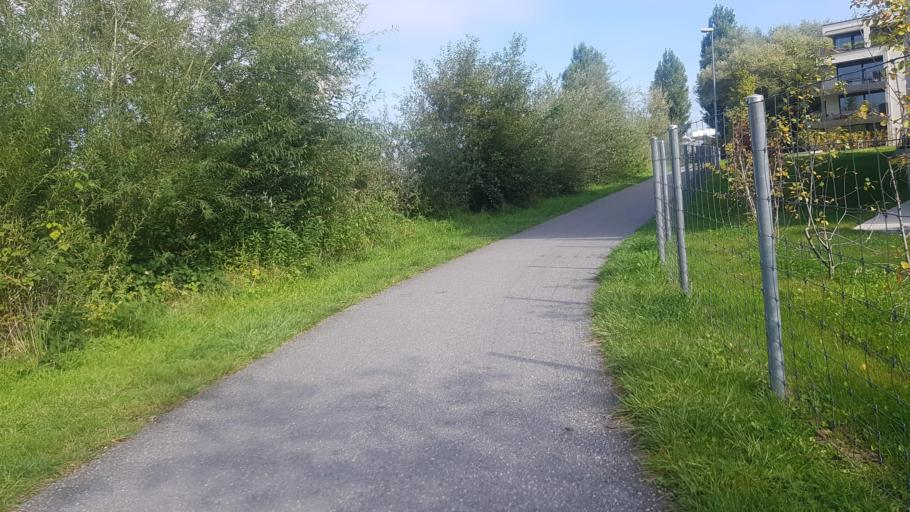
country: CH
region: Appenzell Ausserrhoden
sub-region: Bezirk Vorderland
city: Heiden
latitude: 47.4848
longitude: 9.5435
